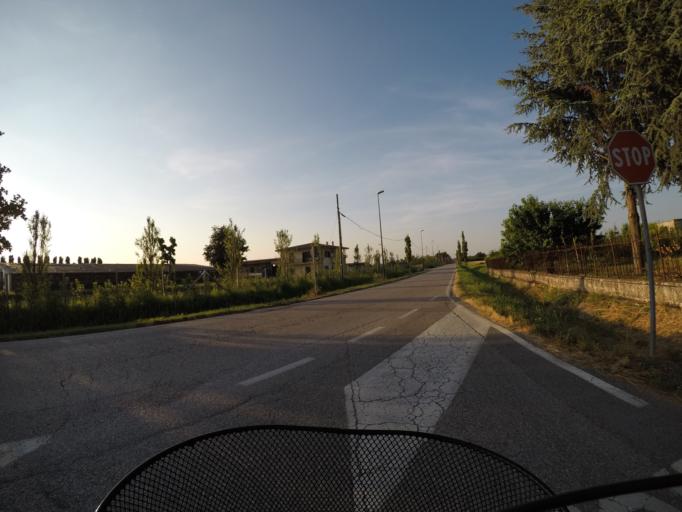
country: IT
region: Veneto
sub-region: Provincia di Rovigo
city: San Bellino
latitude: 45.0198
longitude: 11.5854
